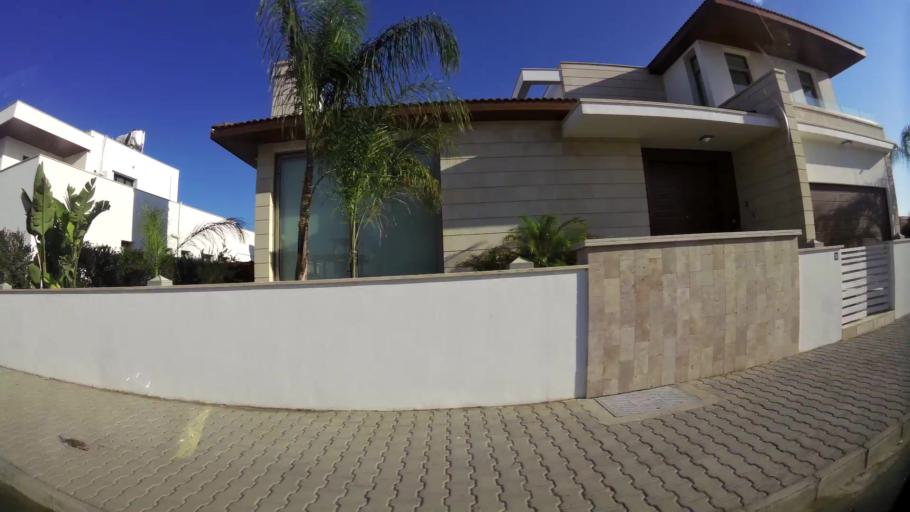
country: CY
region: Lefkosia
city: Nicosia
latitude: 35.2037
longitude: 33.3025
